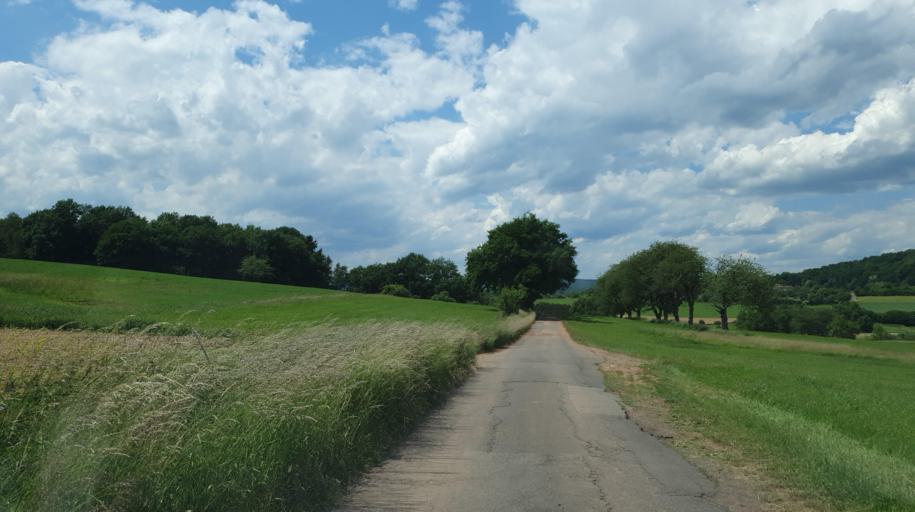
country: DE
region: Saarland
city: Sankt Wendel
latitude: 49.5081
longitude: 7.1779
